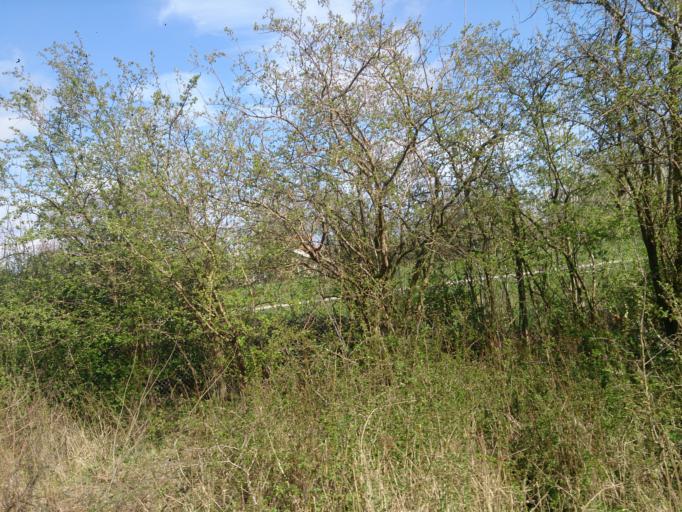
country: DK
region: Capital Region
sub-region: Tarnby Kommune
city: Tarnby
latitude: 55.6173
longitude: 12.5784
